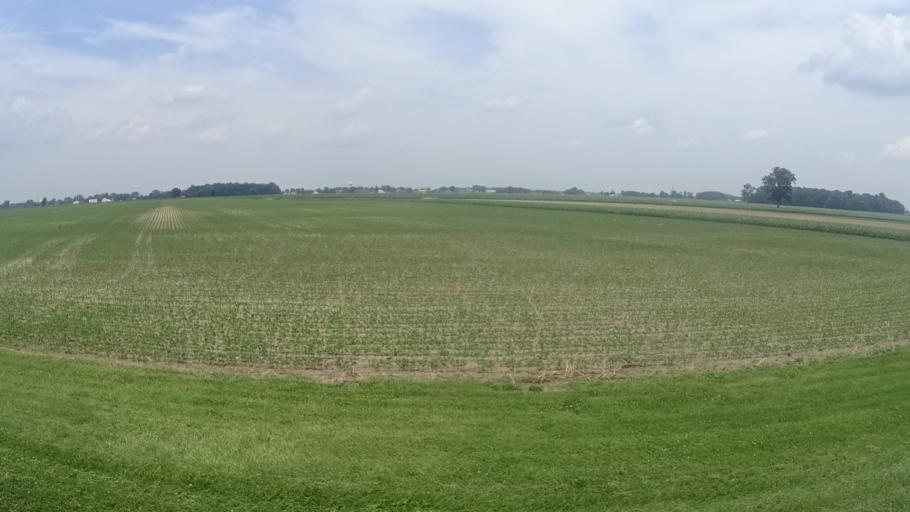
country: US
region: Ohio
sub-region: Erie County
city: Milan
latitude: 41.3082
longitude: -82.6363
